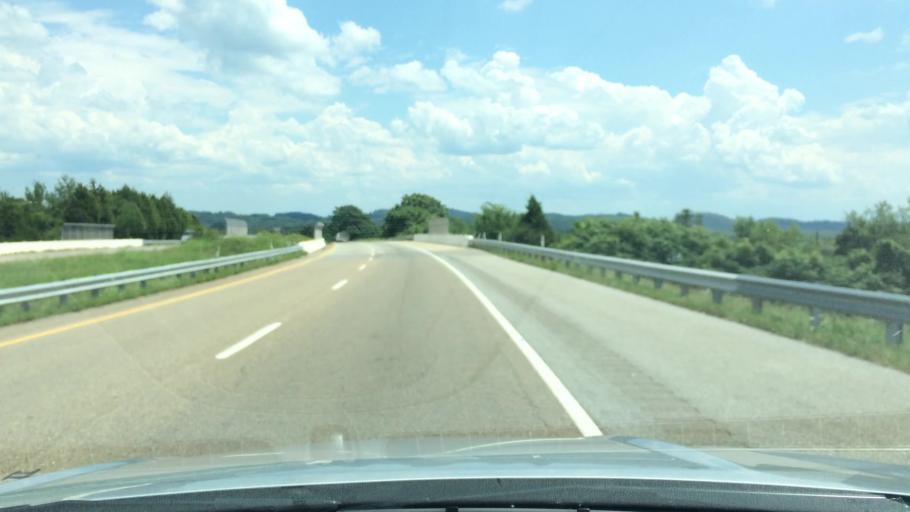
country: US
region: Tennessee
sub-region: Hamblen County
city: Morristown
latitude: 36.1712
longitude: -83.3863
